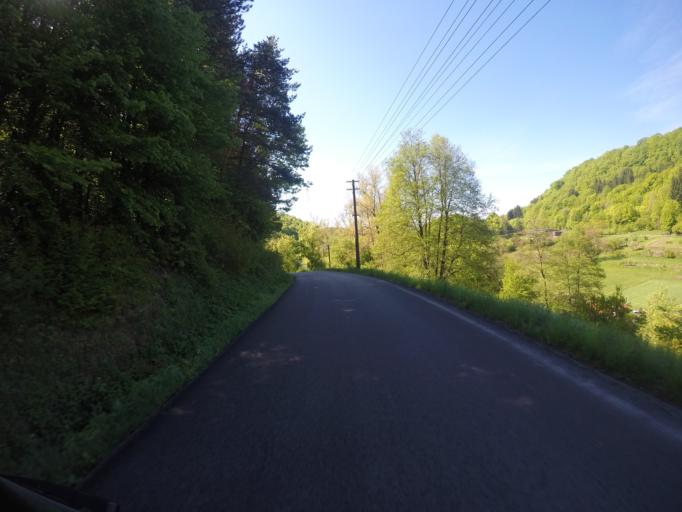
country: SK
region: Banskobystricky
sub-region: Okres Ziar nad Hronom
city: Kremnica
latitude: 48.6091
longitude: 19.0097
